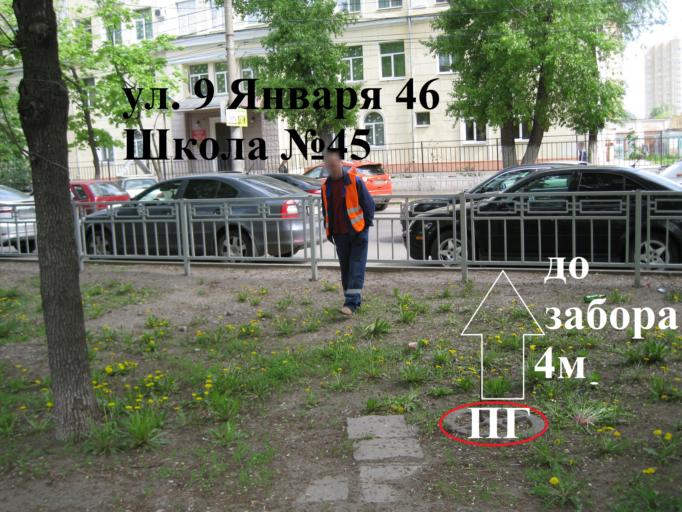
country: RU
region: Voronezj
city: Voronezh
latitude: 51.6634
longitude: 39.1854
